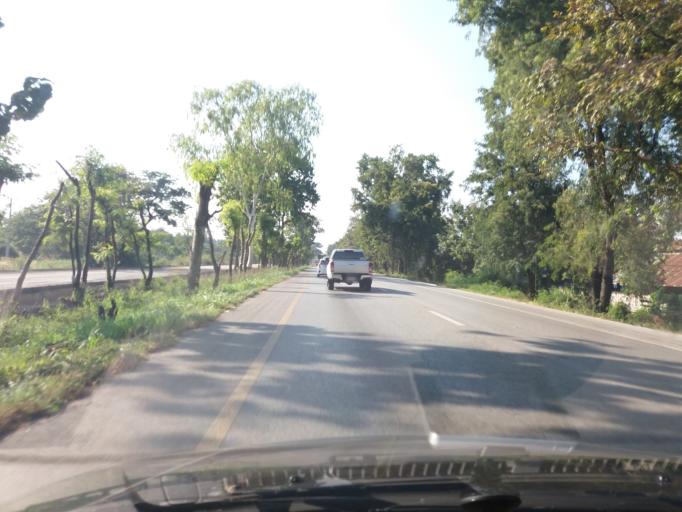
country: TH
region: Nakhon Sawan
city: Nakhon Sawan
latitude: 15.7383
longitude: 100.0194
